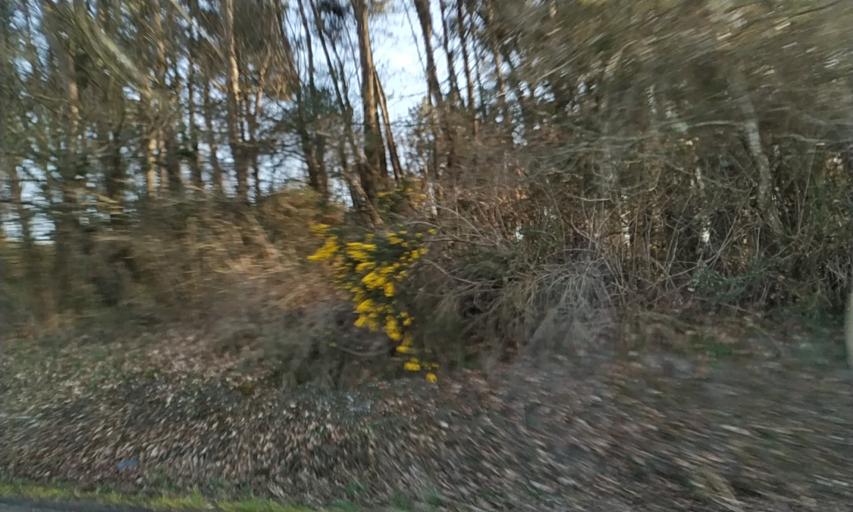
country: ES
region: Galicia
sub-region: Provincia de Lugo
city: Corgo
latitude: 42.9356
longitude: -7.4072
